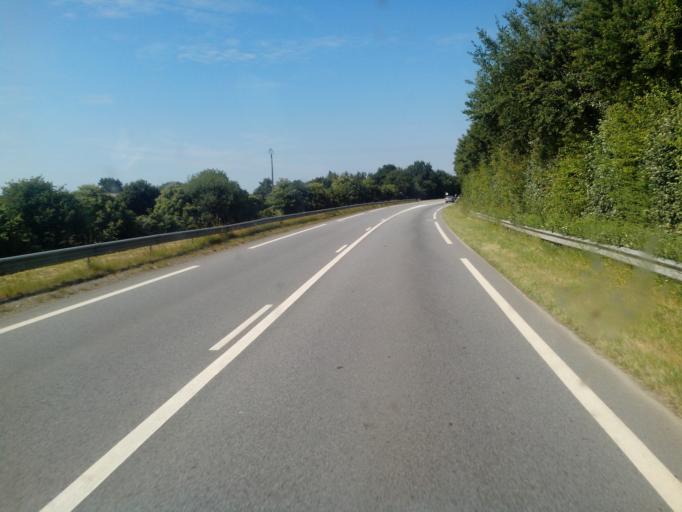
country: FR
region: Brittany
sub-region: Departement d'Ille-et-Vilaine
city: Chevaigne
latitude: 48.2442
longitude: -1.6210
